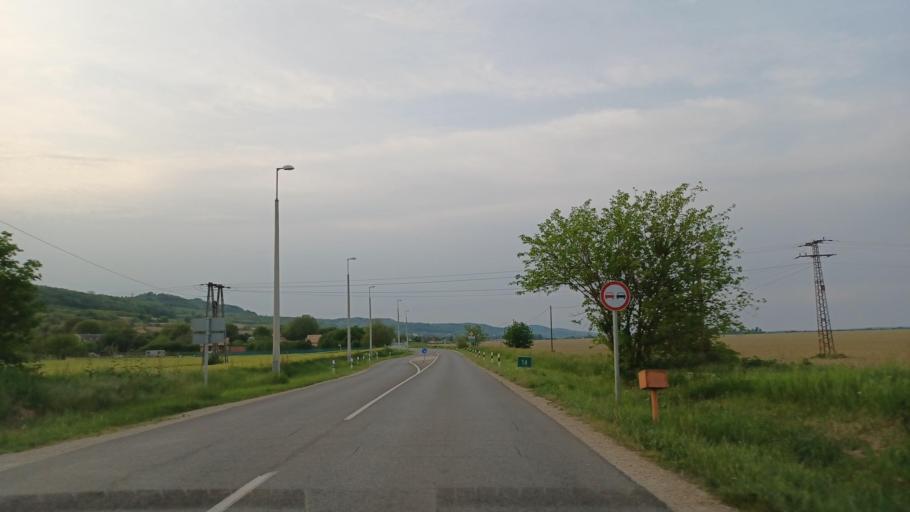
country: HU
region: Tolna
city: Bataszek
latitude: 46.2585
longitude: 18.6850
